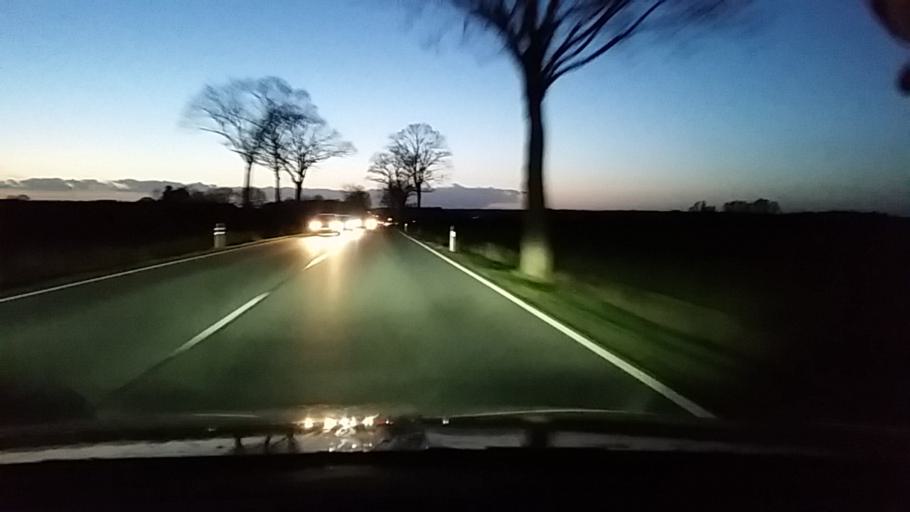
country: DE
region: Lower Saxony
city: Calberlah
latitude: 52.3942
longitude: 10.6379
